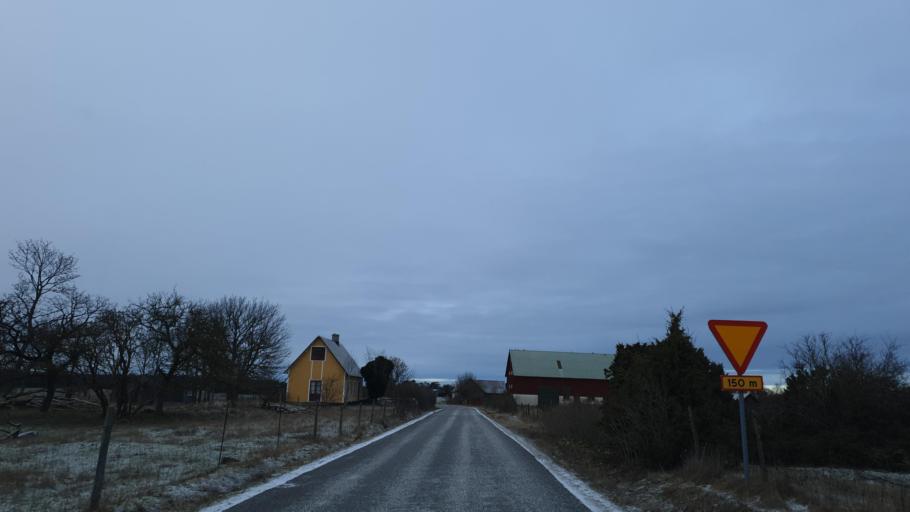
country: SE
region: Gotland
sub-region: Gotland
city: Slite
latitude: 57.3938
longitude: 18.8077
